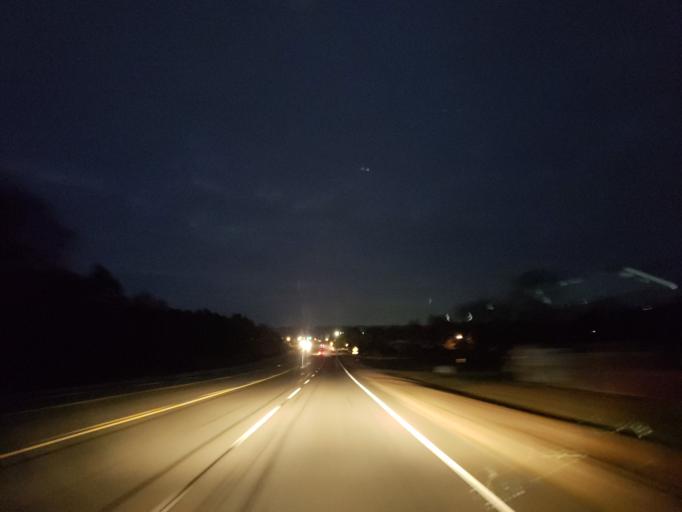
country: US
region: Georgia
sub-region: Polk County
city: Rockmart
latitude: 34.0132
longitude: -85.0267
